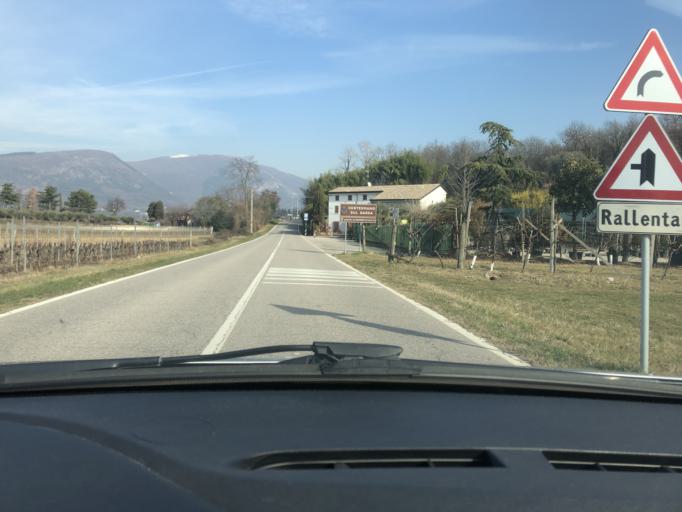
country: IT
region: Veneto
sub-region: Provincia di Verona
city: Costermano
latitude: 45.5691
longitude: 10.7384
